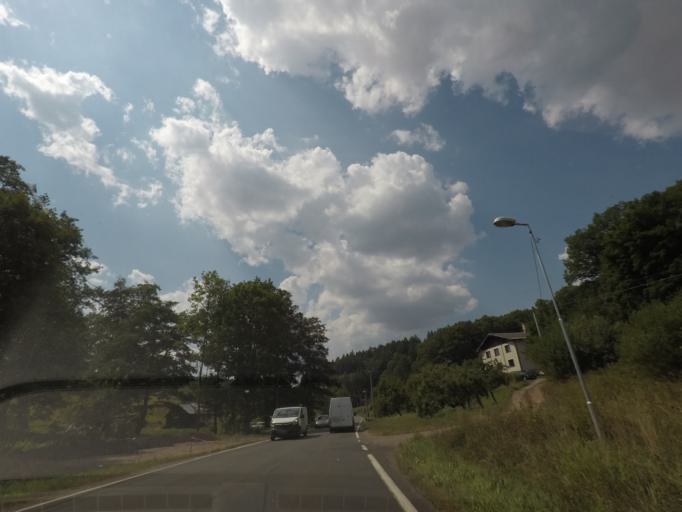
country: CZ
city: Velke Svatonovice
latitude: 50.5926
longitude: 15.9899
